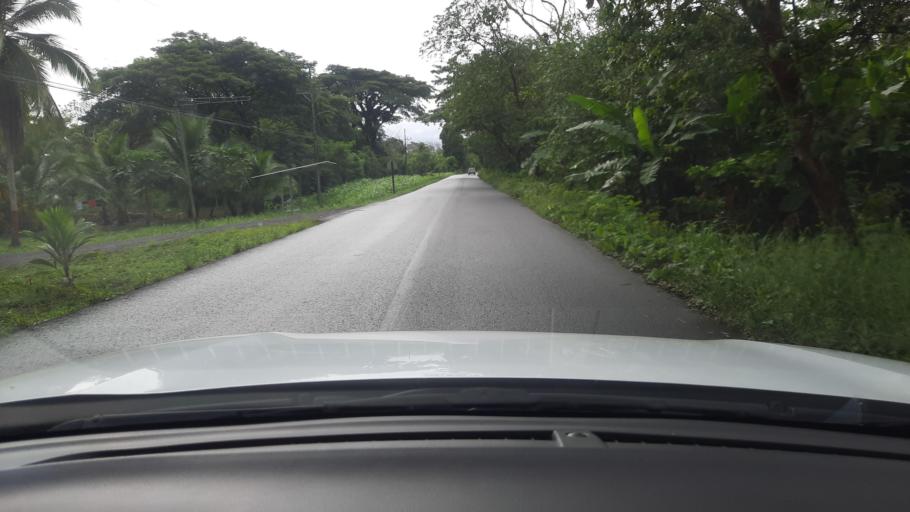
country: CR
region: Alajuela
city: San Jose
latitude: 10.9293
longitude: -85.0859
